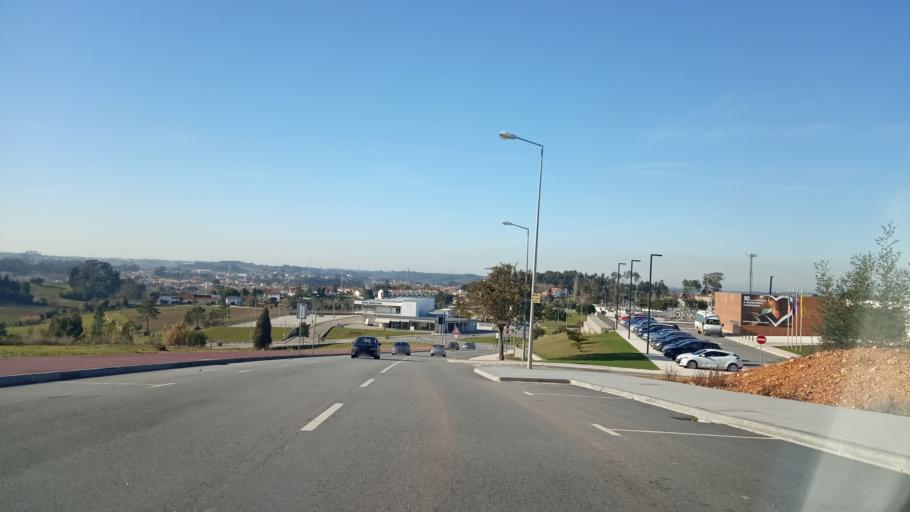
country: PT
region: Aveiro
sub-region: Anadia
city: Anadia
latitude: 40.4343
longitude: -8.4395
